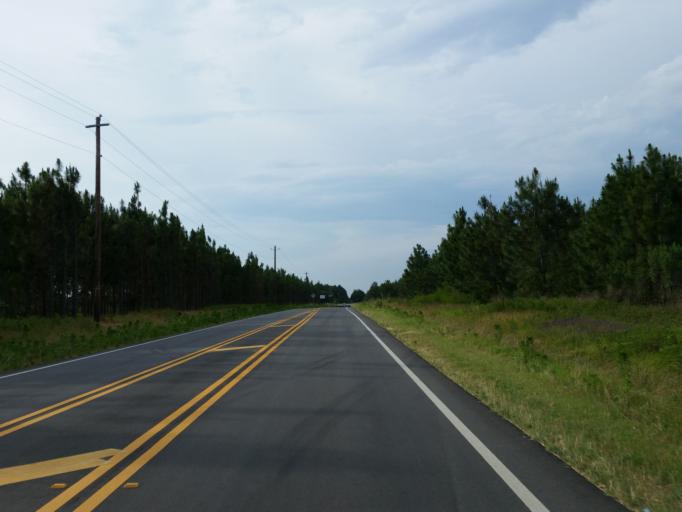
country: US
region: Georgia
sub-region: Turner County
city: Ashburn
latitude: 31.7253
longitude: -83.6649
